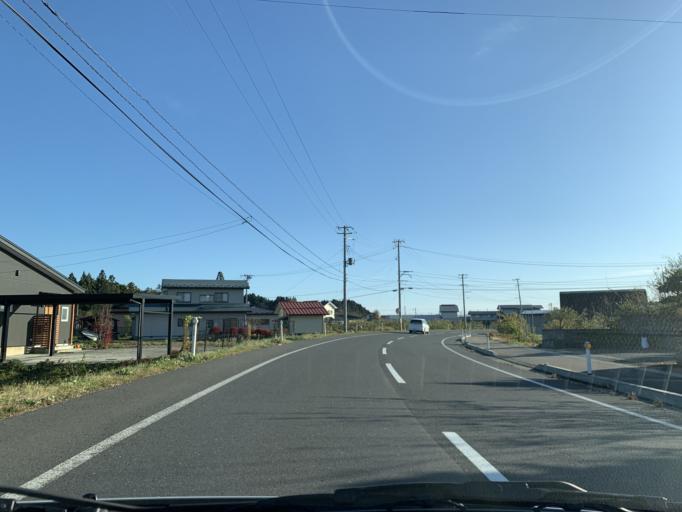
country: JP
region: Iwate
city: Kitakami
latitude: 39.2291
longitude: 141.1285
